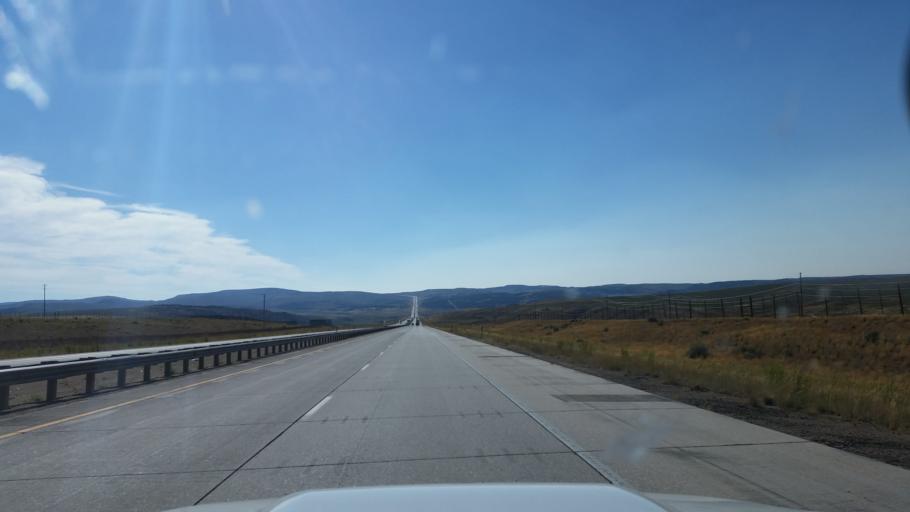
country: US
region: Wyoming
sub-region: Uinta County
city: Mountain View
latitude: 41.2980
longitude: -110.5936
